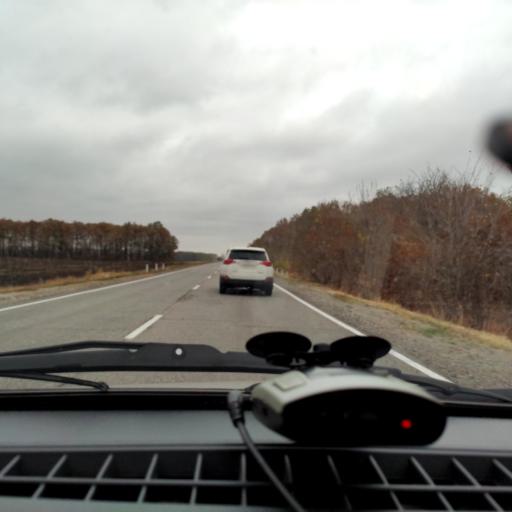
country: RU
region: Voronezj
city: Shilovo
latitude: 51.4179
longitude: 39.0064
